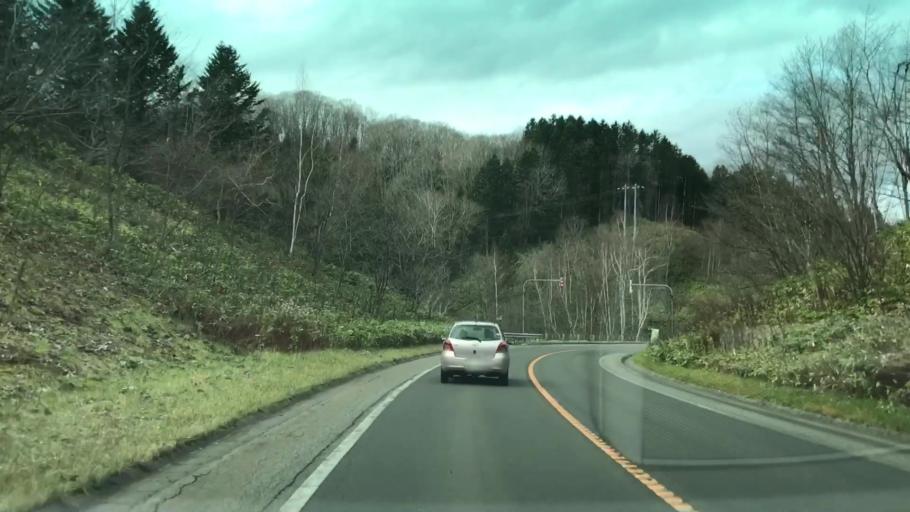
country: JP
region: Hokkaido
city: Shimo-furano
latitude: 42.9211
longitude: 142.4454
